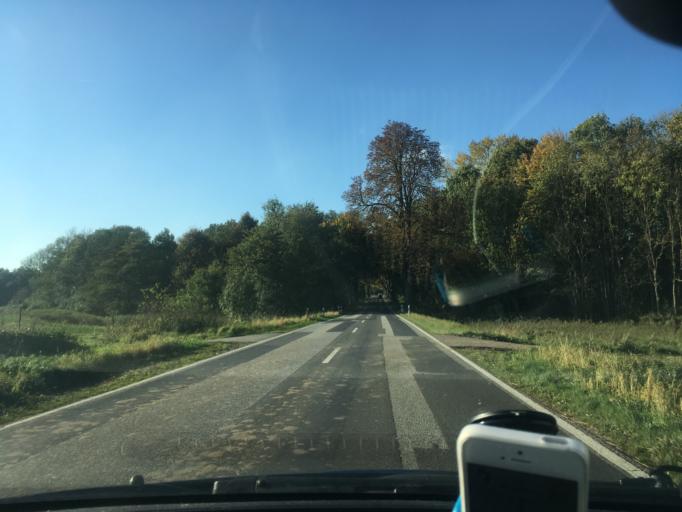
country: DE
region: Mecklenburg-Vorpommern
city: Zarrentin
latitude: 53.5243
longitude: 10.9863
